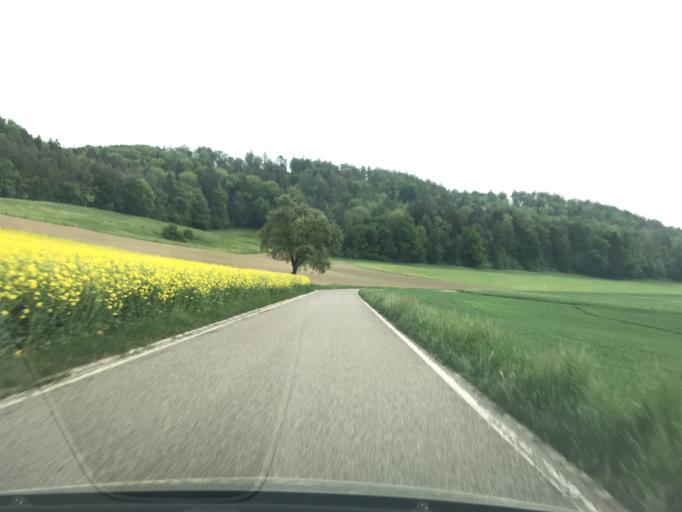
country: CH
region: Zurich
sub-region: Bezirk Winterthur
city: Wuelflingen (Kreis 6) / Niederfeld
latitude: 47.4952
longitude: 8.6840
